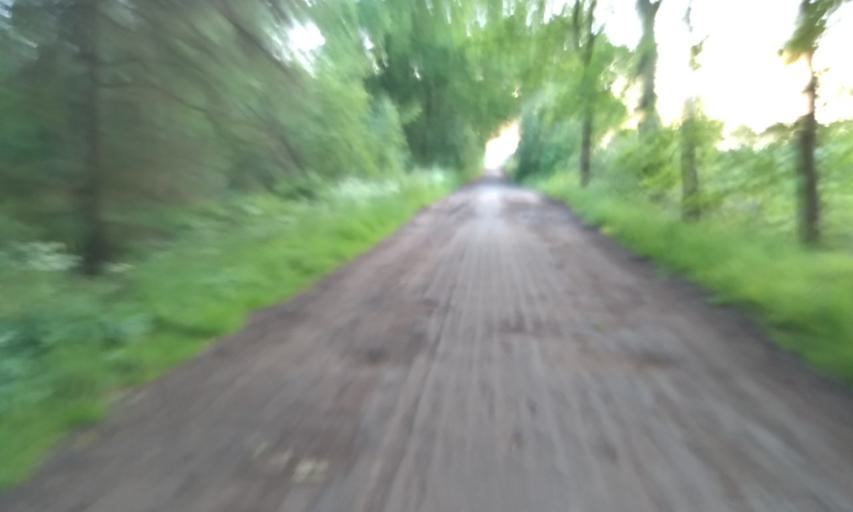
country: DE
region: Lower Saxony
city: Dollern
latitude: 53.5301
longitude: 9.5432
